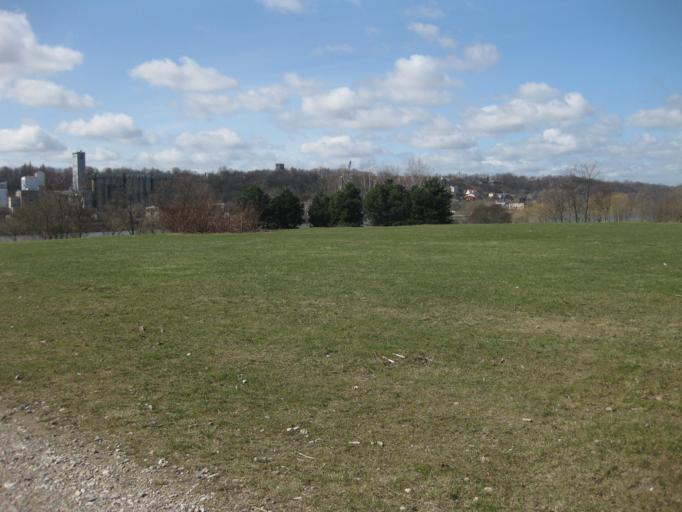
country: LT
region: Kauno apskritis
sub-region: Kaunas
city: Aleksotas
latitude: 54.8915
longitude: 23.9066
